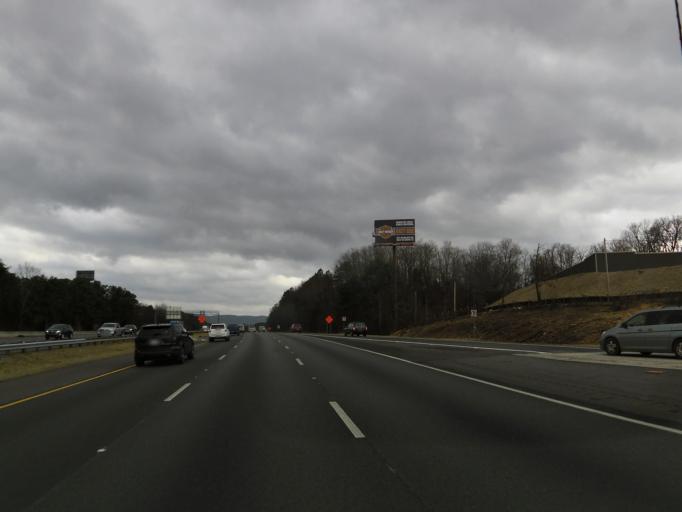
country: US
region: Georgia
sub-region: Catoosa County
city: Indian Springs
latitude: 34.9261
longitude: -85.1516
